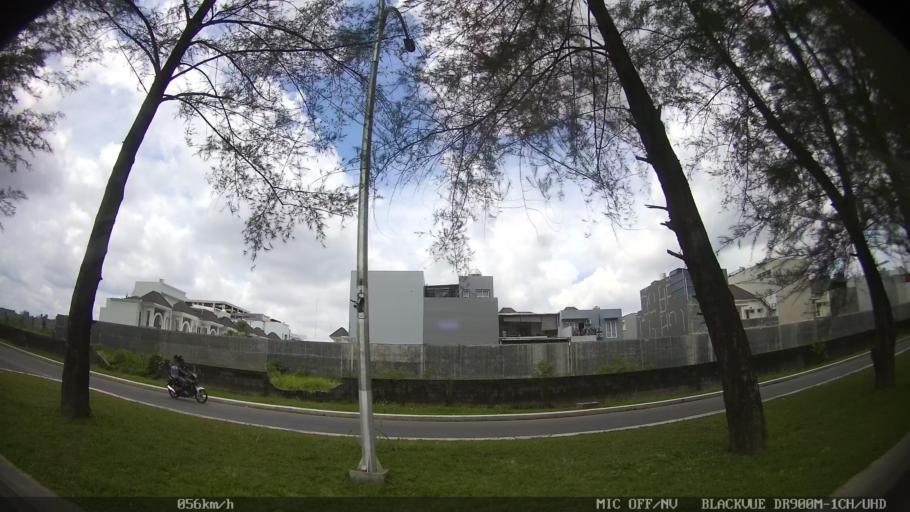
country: ID
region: North Sumatra
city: Medan
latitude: 3.6115
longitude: 98.7291
